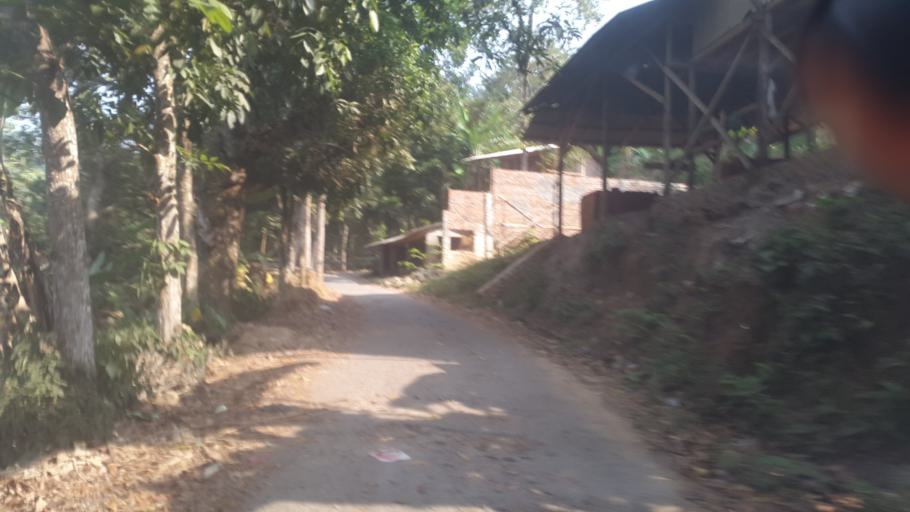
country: ID
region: West Java
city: Tugu
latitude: -6.9450
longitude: 106.4469
